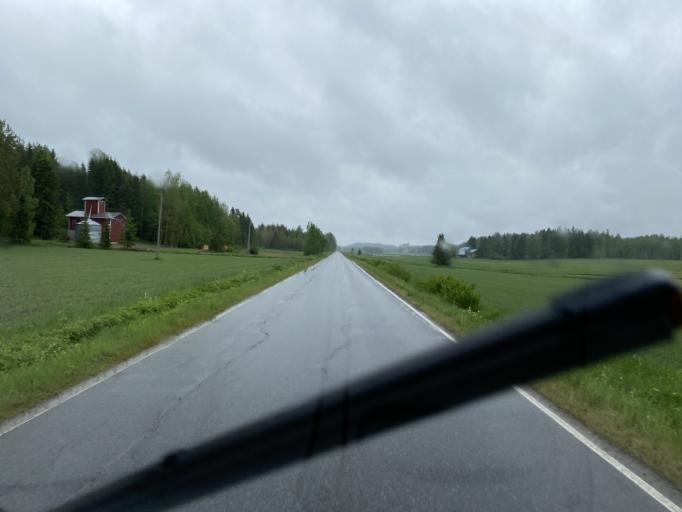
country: FI
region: Haeme
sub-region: Forssa
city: Humppila
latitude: 61.0466
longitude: 23.3734
